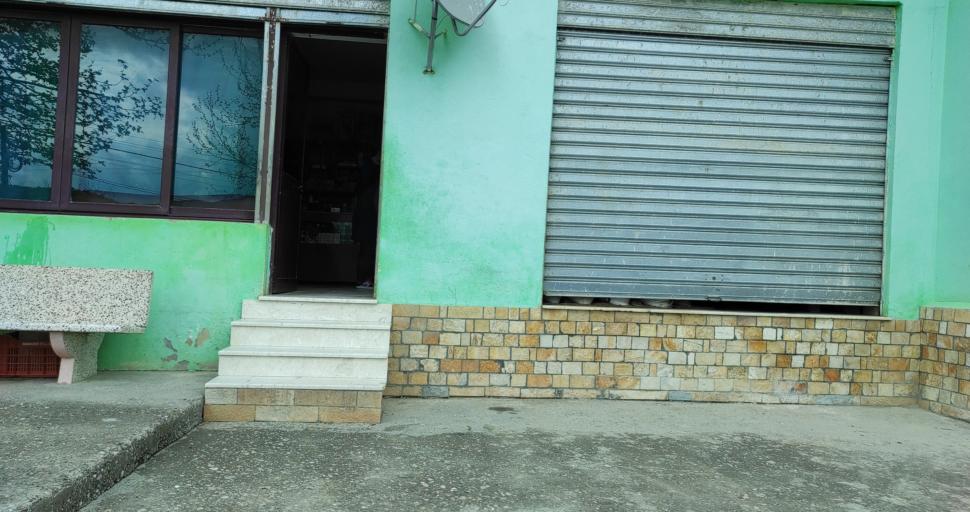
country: AL
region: Shkoder
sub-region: Rrethi i Shkodres
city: Dajc
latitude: 42.0319
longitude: 19.4146
